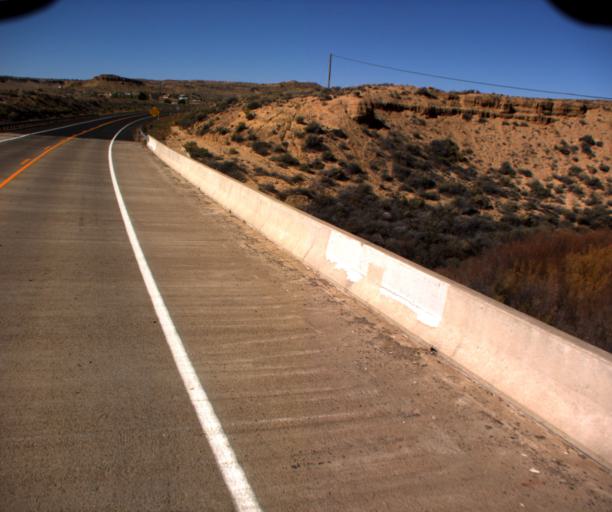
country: US
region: Arizona
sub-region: Navajo County
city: First Mesa
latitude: 35.8735
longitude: -110.6018
